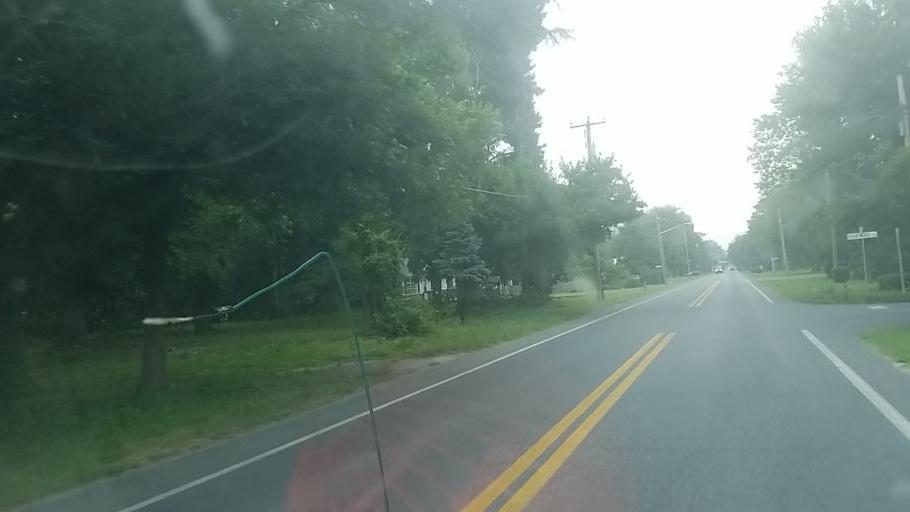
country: US
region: Maryland
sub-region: Wicomico County
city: Salisbury
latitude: 38.3735
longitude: -75.5460
